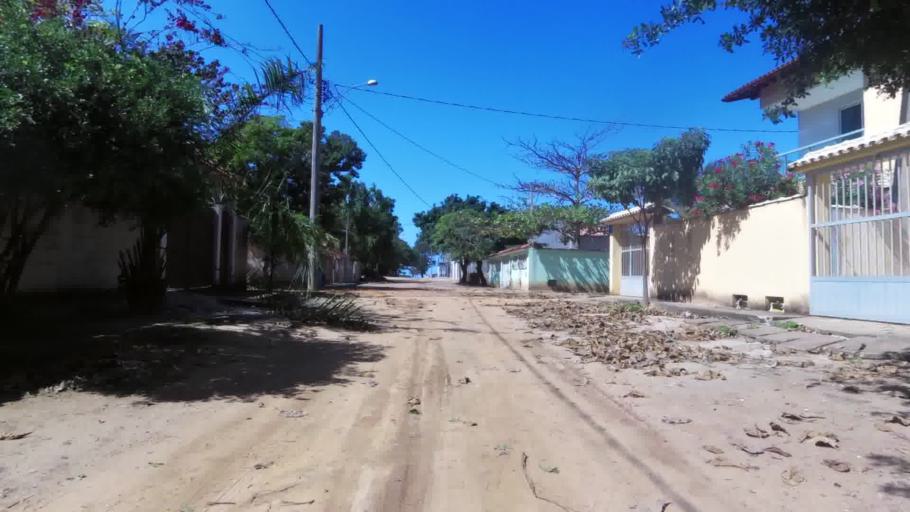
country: BR
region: Espirito Santo
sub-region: Piuma
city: Piuma
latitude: -20.8364
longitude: -40.6295
